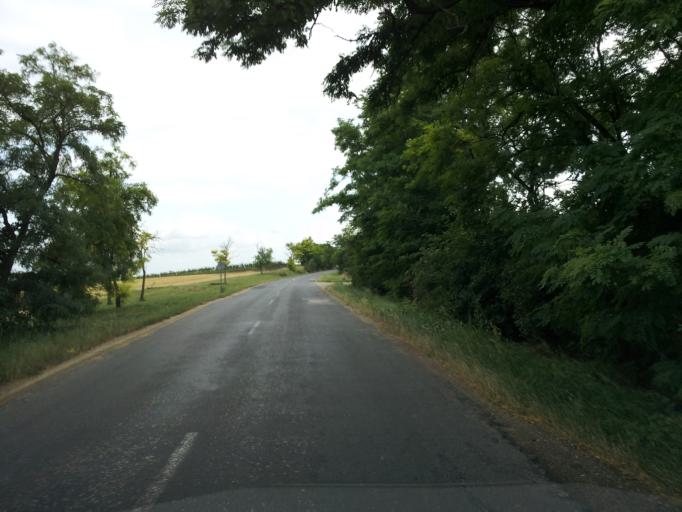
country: HU
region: Fejer
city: Enying
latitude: 46.9043
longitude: 18.2581
